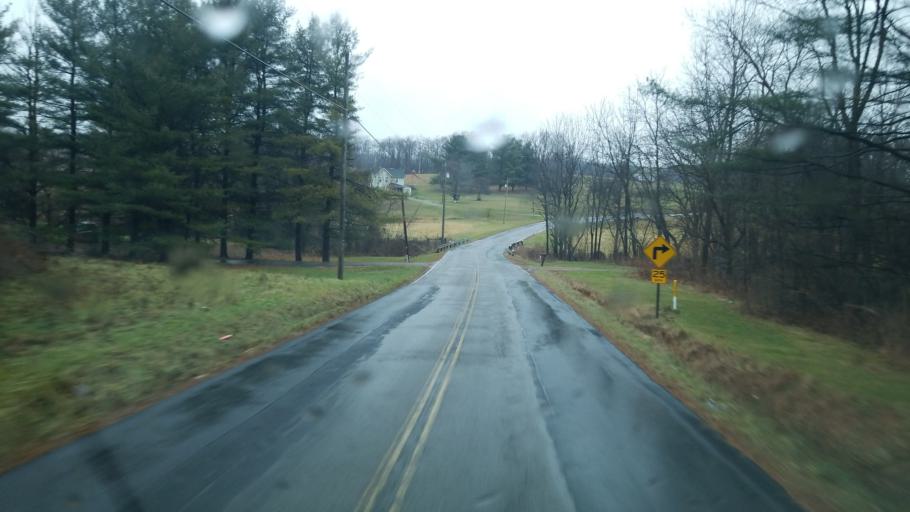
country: US
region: Ohio
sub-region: Licking County
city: Newark
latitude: 40.0736
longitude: -82.3659
